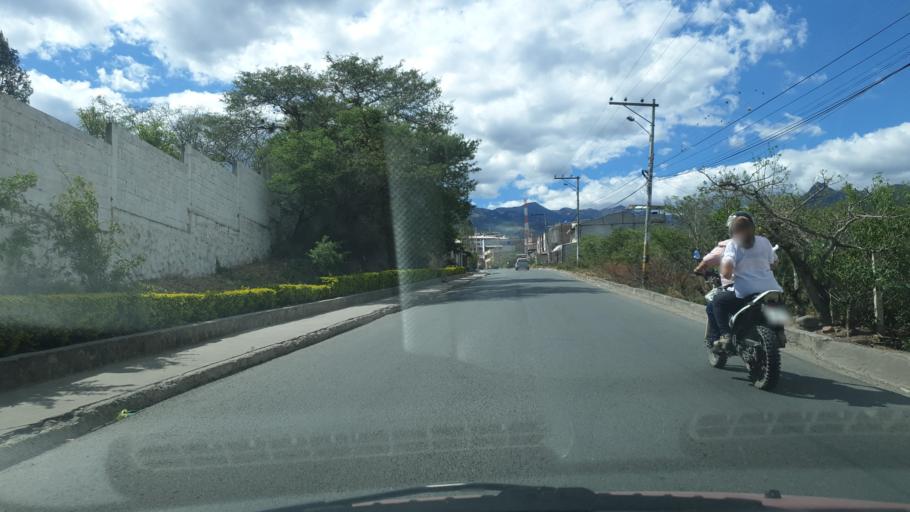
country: EC
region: Azuay
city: Cuenca
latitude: -3.2797
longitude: -79.3135
